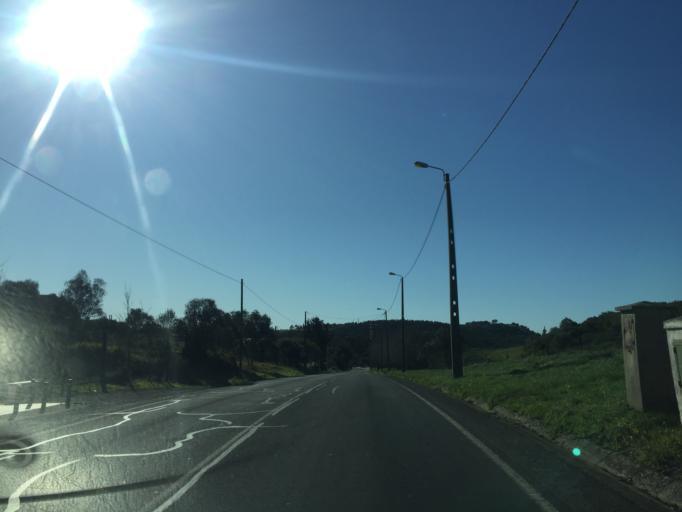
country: PT
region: Lisbon
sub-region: Sintra
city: Almargem
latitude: 38.8189
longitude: -9.2915
